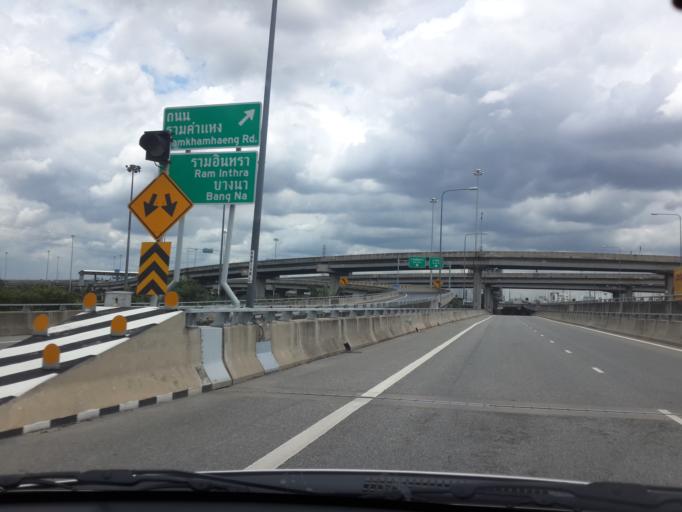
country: TH
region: Bangkok
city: Watthana
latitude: 13.7520
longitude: 100.5926
